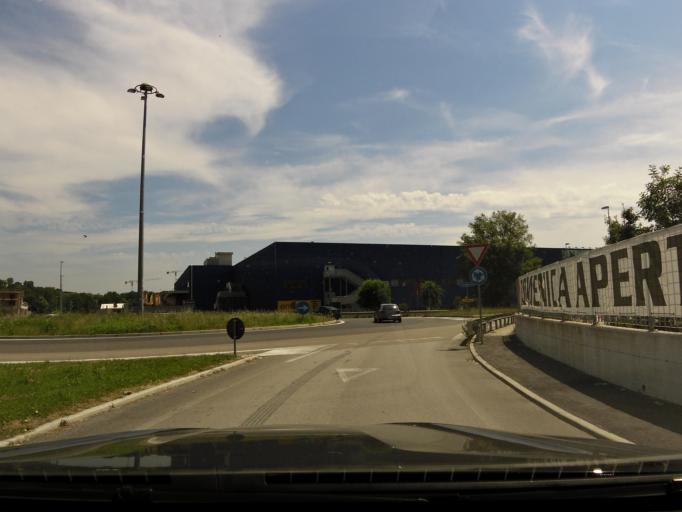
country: IT
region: The Marches
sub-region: Provincia di Ancona
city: San Biagio
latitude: 43.5299
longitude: 13.5170
